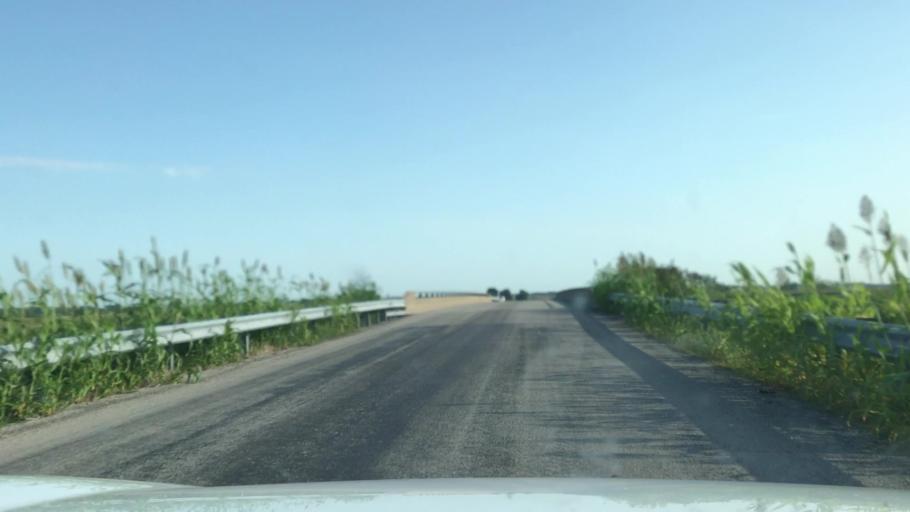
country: US
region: Illinois
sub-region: Washington County
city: Okawville
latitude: 38.4282
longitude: -89.4778
